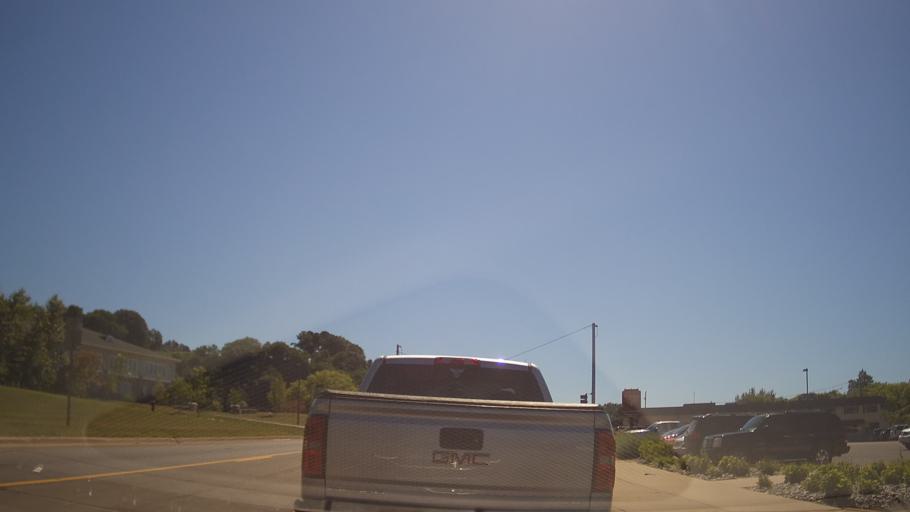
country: US
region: Michigan
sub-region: Emmet County
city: Petoskey
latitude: 45.3817
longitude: -84.9434
